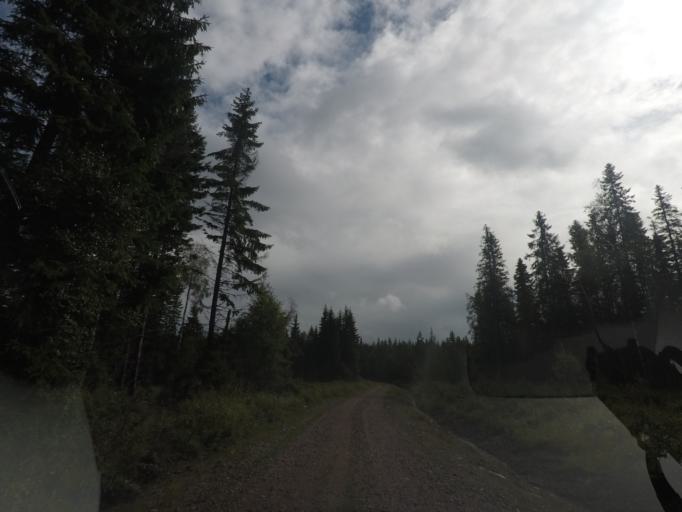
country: SE
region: Vaermland
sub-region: Filipstads Kommun
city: Lesjofors
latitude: 60.0944
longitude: 14.3767
